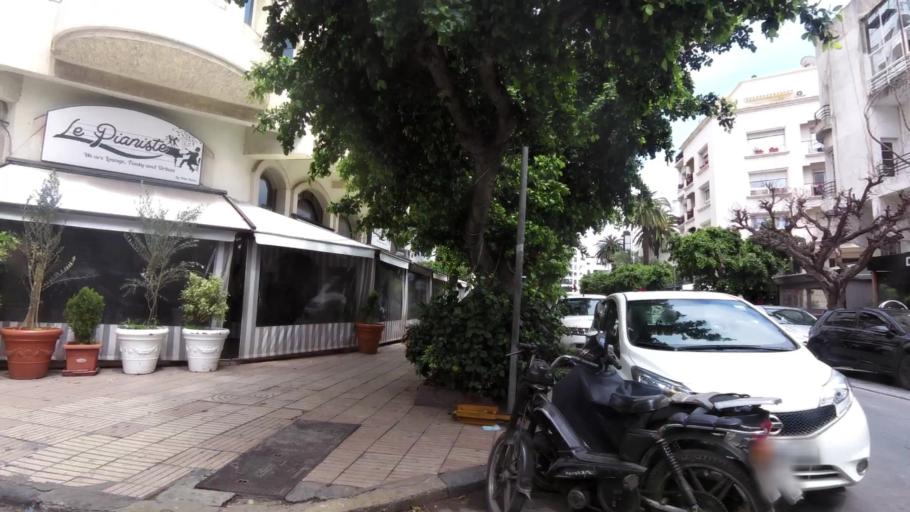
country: MA
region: Grand Casablanca
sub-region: Casablanca
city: Casablanca
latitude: 33.5927
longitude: -7.6298
